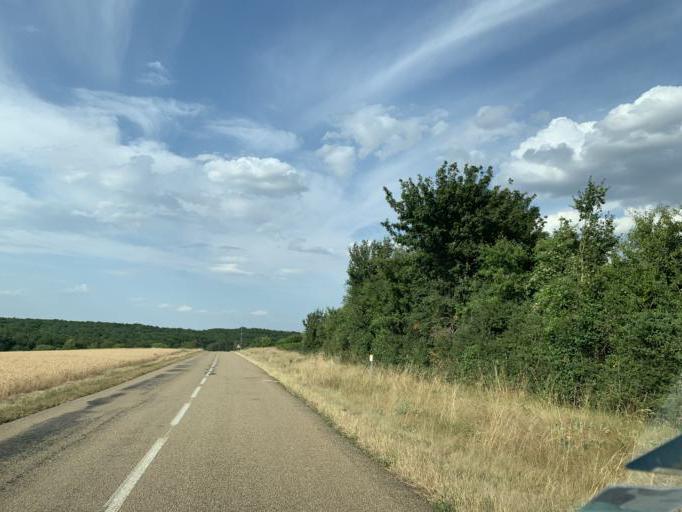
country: FR
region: Bourgogne
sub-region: Departement de l'Yonne
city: Fontenailles
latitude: 47.5277
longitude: 3.3873
